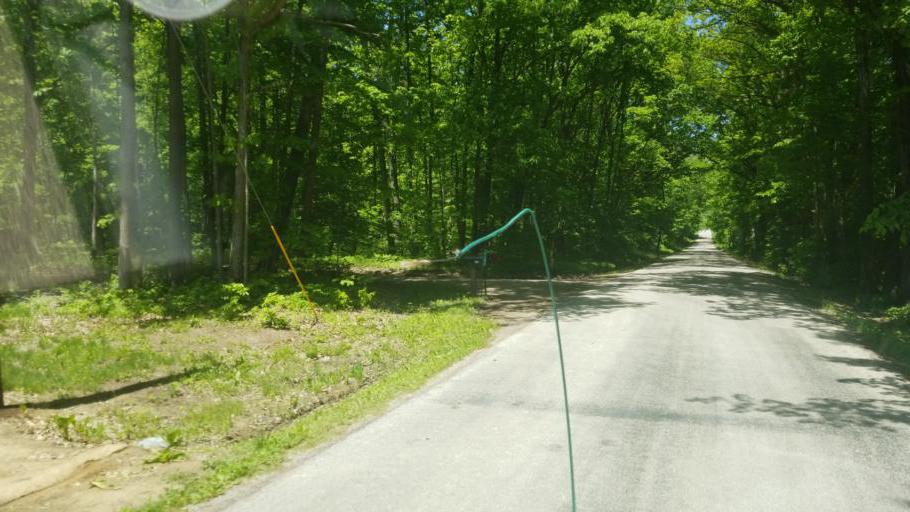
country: US
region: Ohio
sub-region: Huron County
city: Greenwich
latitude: 40.9830
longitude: -82.4321
